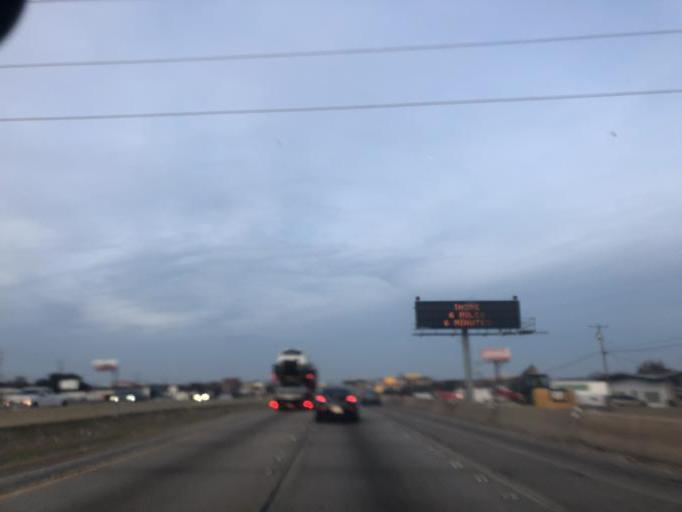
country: US
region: Texas
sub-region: Dallas County
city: Duncanville
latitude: 32.6358
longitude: -96.8969
